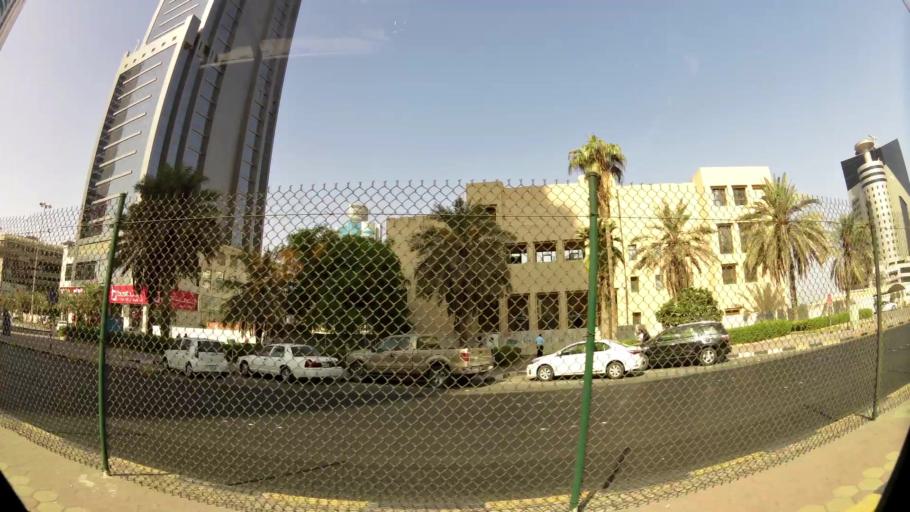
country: KW
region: Al Asimah
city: Kuwait City
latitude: 29.3634
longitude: 47.9649
